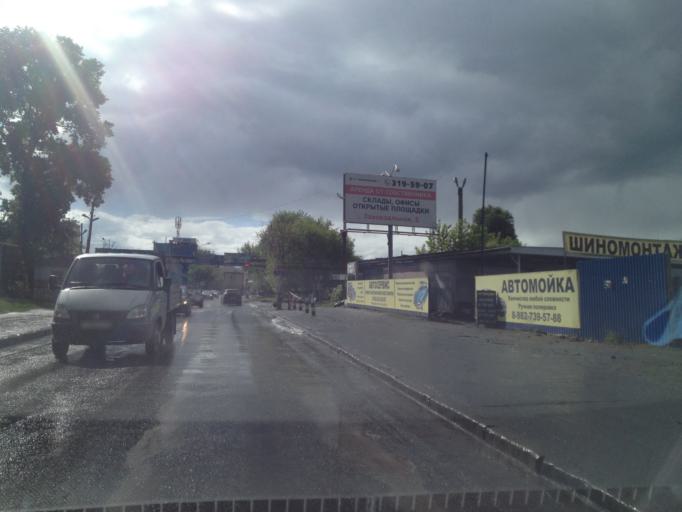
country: RU
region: Sverdlovsk
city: Yekaterinburg
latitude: 56.8631
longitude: 60.6044
